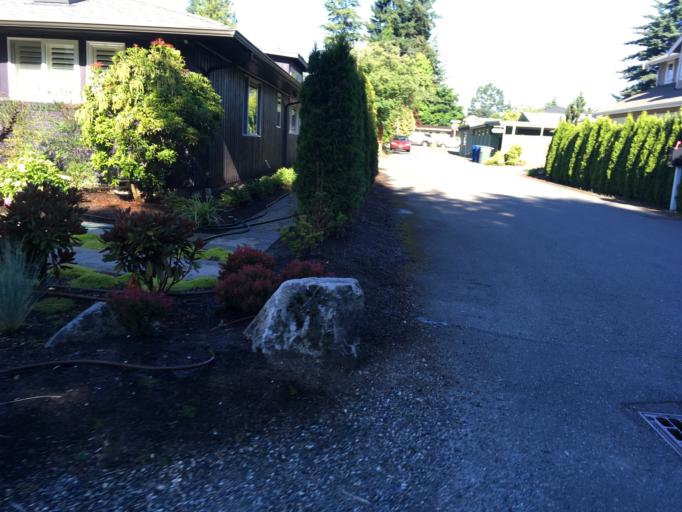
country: US
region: Washington
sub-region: King County
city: Bellevue
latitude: 47.6219
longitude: -122.1953
